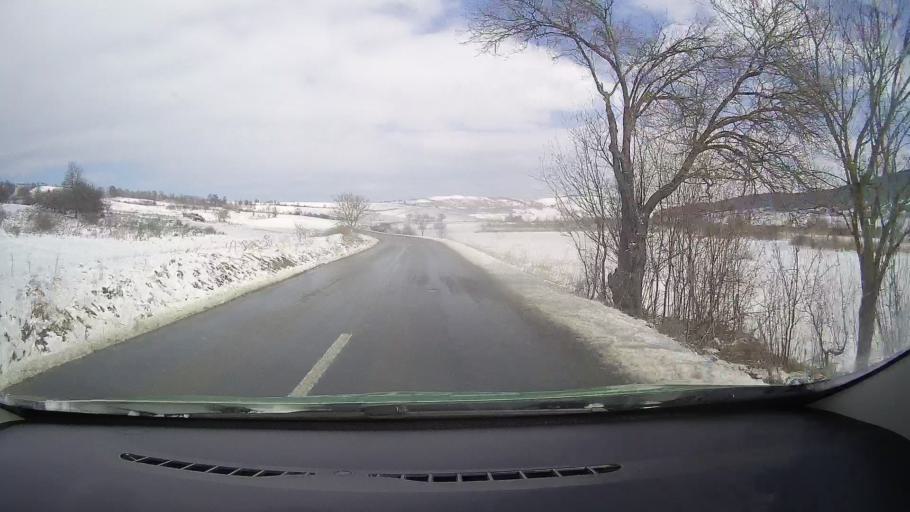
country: RO
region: Sibiu
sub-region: Comuna Altina
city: Altina
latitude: 45.9587
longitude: 24.4557
